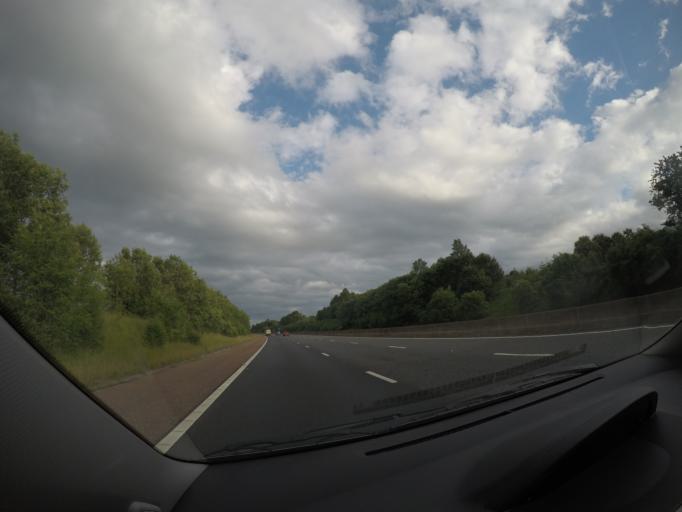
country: GB
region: England
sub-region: Cumbria
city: Penrith
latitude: 54.6833
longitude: -2.7879
